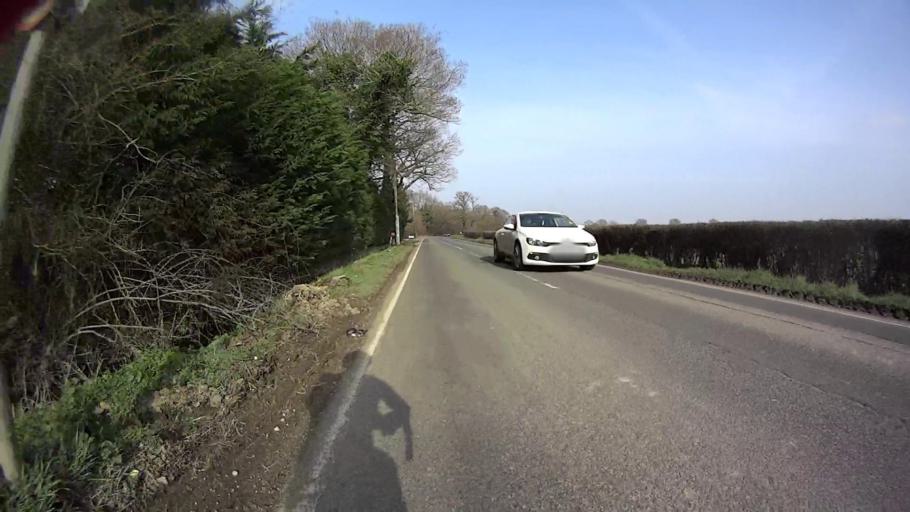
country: GB
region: England
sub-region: West Sussex
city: Copthorne
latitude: 51.1766
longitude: -0.0912
